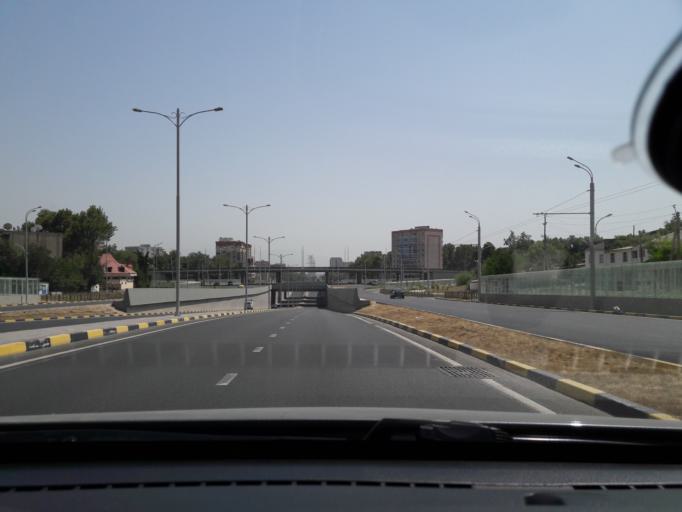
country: TJ
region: Dushanbe
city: Dushanbe
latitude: 38.5856
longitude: 68.7410
